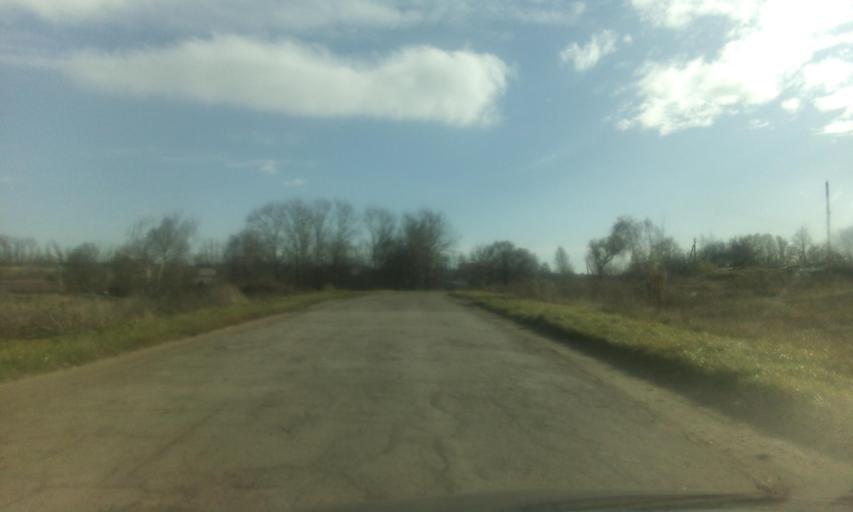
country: RU
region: Tula
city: Dubovka
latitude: 53.9455
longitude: 38.0359
